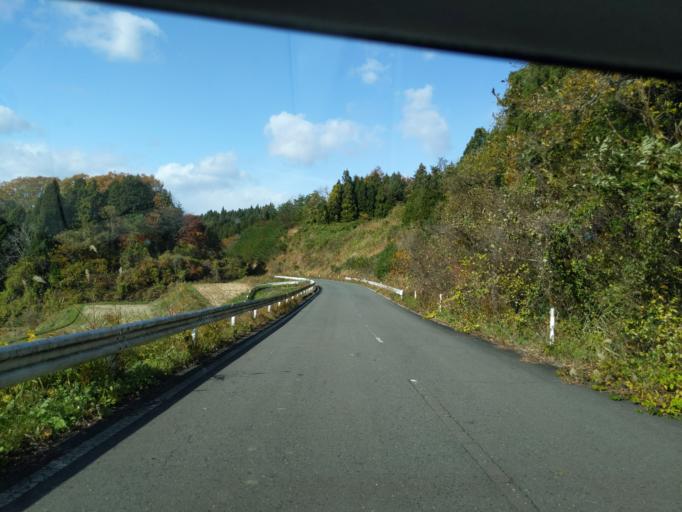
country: JP
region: Iwate
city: Mizusawa
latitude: 39.0342
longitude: 141.0820
